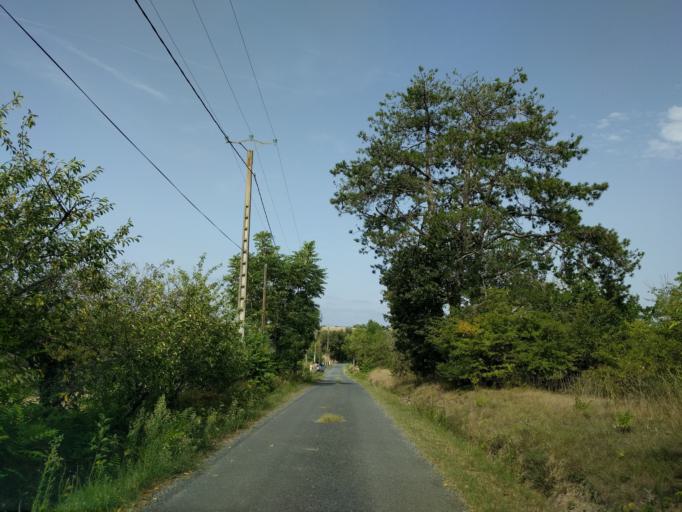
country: FR
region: Midi-Pyrenees
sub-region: Departement du Tarn
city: Saix
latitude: 43.6360
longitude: 2.1905
